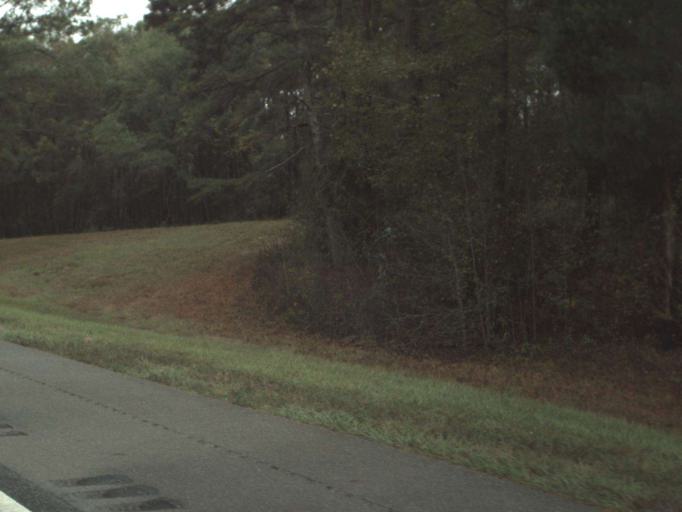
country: US
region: Florida
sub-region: Gadsden County
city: Midway
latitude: 30.5272
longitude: -84.4998
